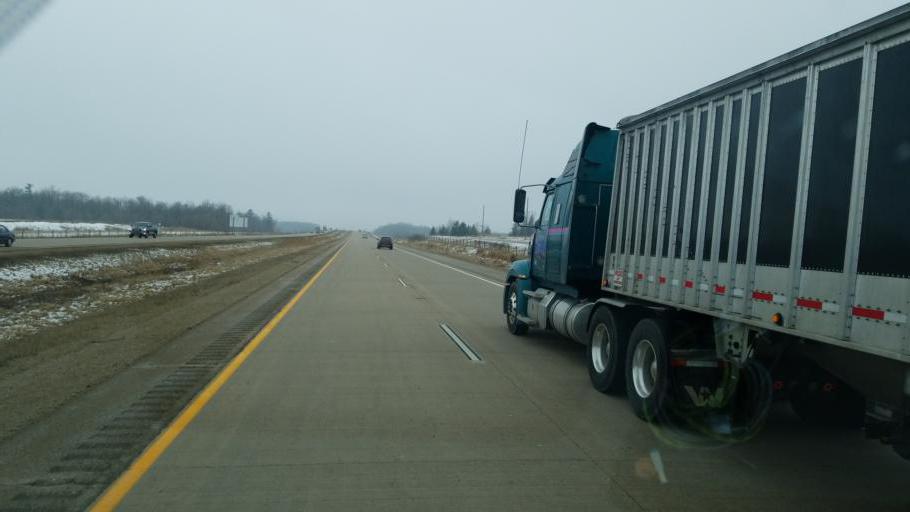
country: US
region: Wisconsin
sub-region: Winnebago County
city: Winneconne
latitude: 44.2343
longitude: -88.7550
